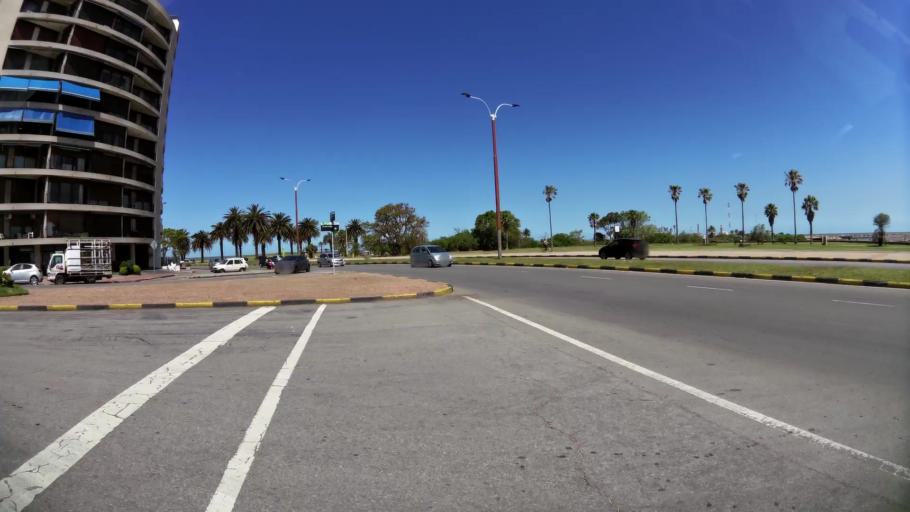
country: UY
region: Montevideo
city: Montevideo
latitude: -34.9289
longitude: -56.1615
